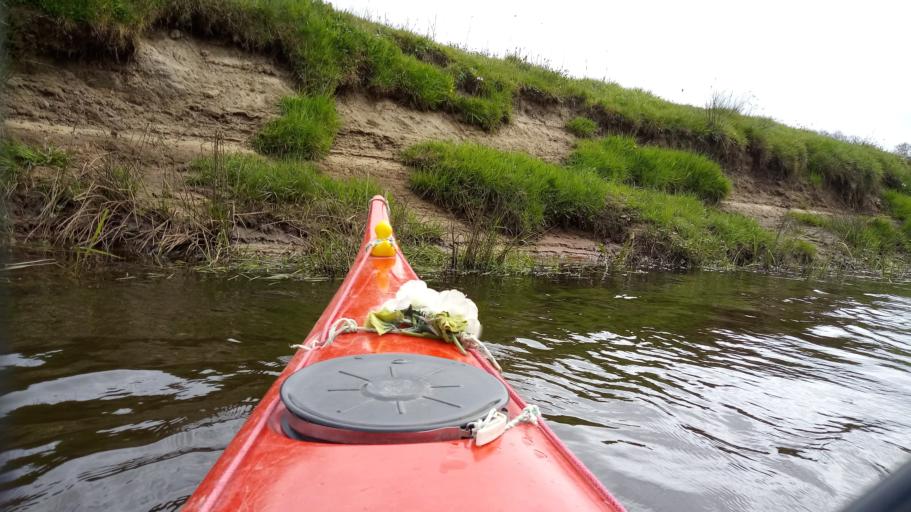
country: NL
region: Overijssel
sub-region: Gemeente Twenterand
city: Den Ham
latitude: 52.4864
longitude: 6.4354
